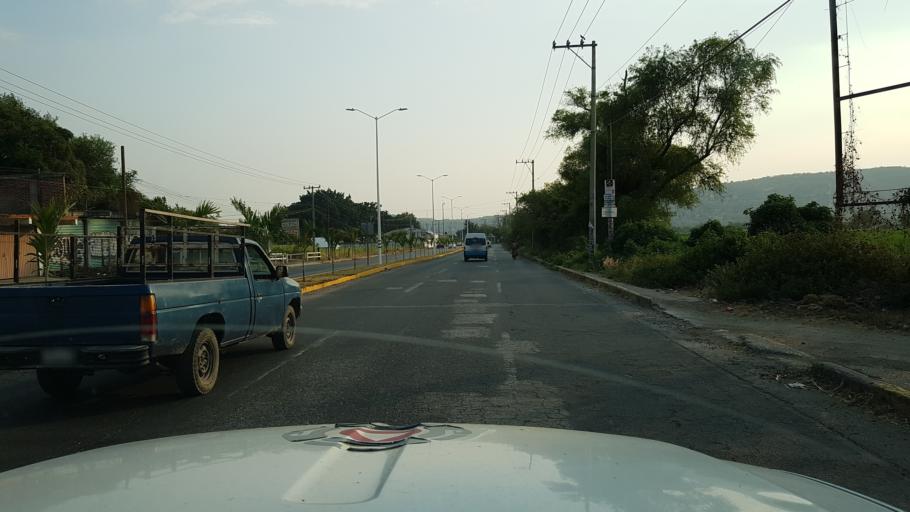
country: MX
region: Morelos
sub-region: Ayala
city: San Pedro Apatlaco
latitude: 18.7950
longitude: -98.9727
